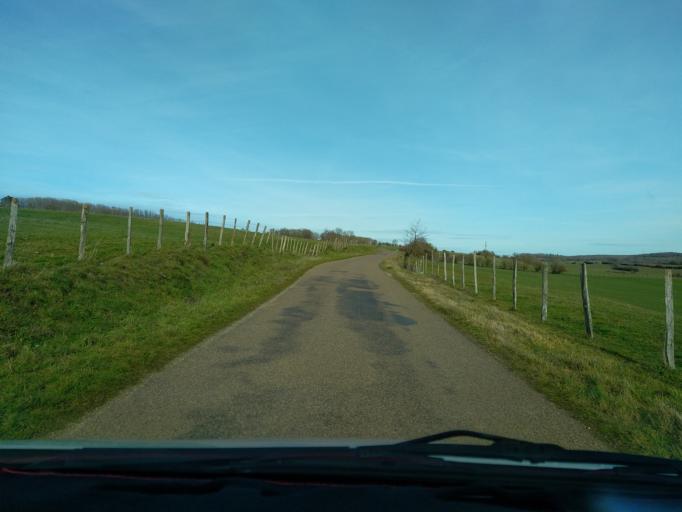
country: FR
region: Franche-Comte
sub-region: Departement de la Haute-Saone
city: Marnay
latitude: 47.3035
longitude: 5.6699
